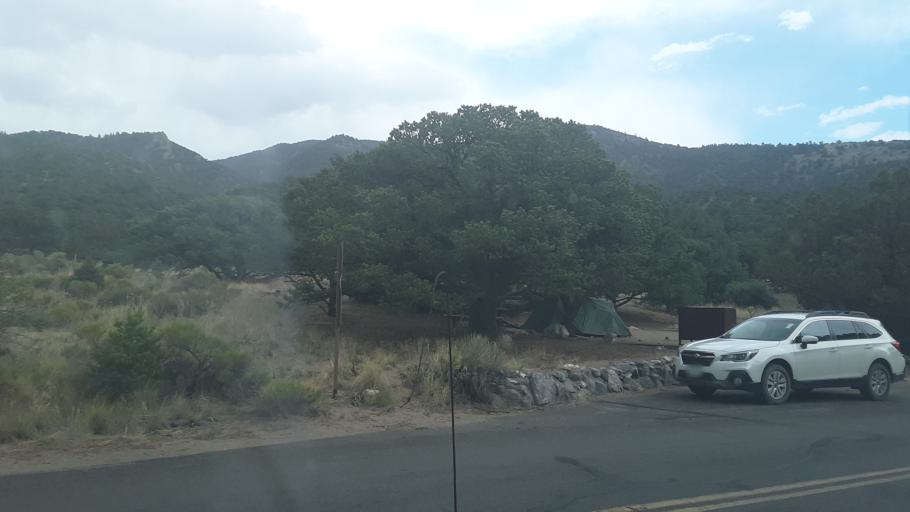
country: US
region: Colorado
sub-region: Custer County
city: Westcliffe
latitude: 37.7453
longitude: -105.5044
